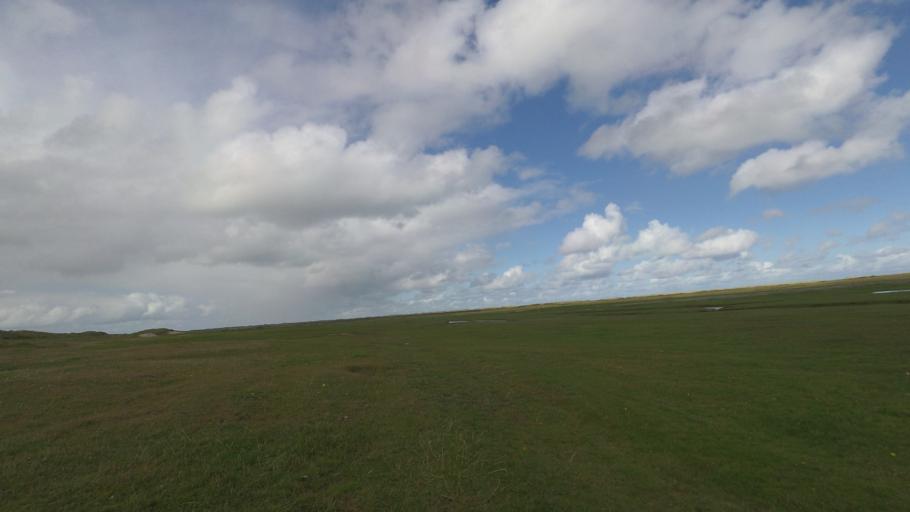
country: NL
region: Friesland
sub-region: Gemeente Ameland
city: Nes
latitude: 53.4492
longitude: 5.8623
